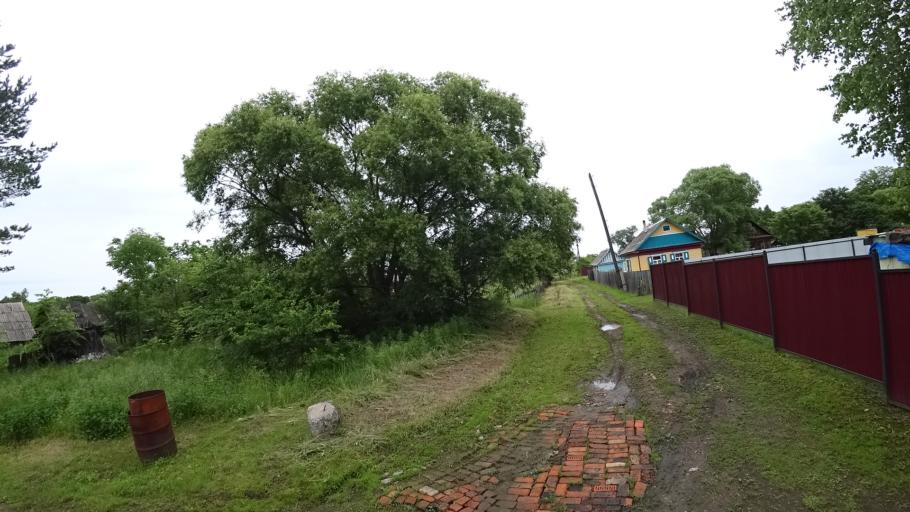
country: RU
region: Primorskiy
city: Novosysoyevka
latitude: 44.2075
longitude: 133.3346
